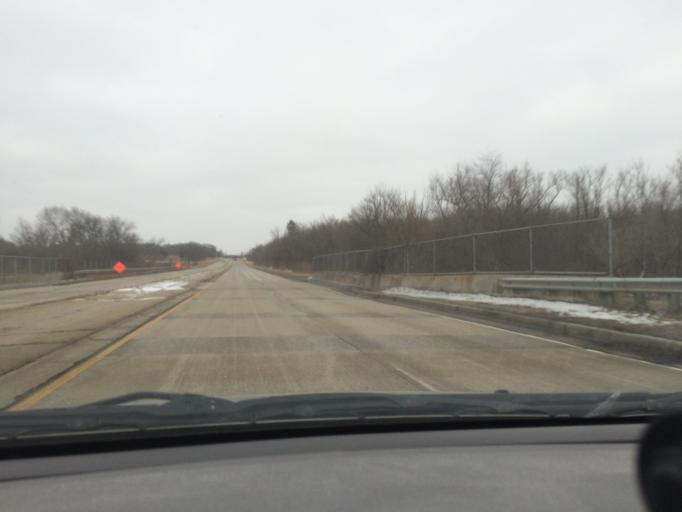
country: US
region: Illinois
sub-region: Cook County
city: Streamwood
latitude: 42.0451
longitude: -88.1791
